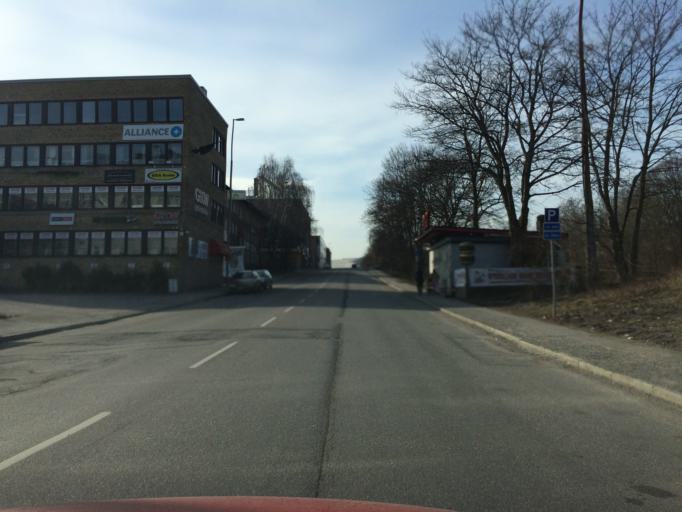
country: SE
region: Stockholm
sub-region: Stockholms Kommun
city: Arsta
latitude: 59.2955
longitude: 18.0117
